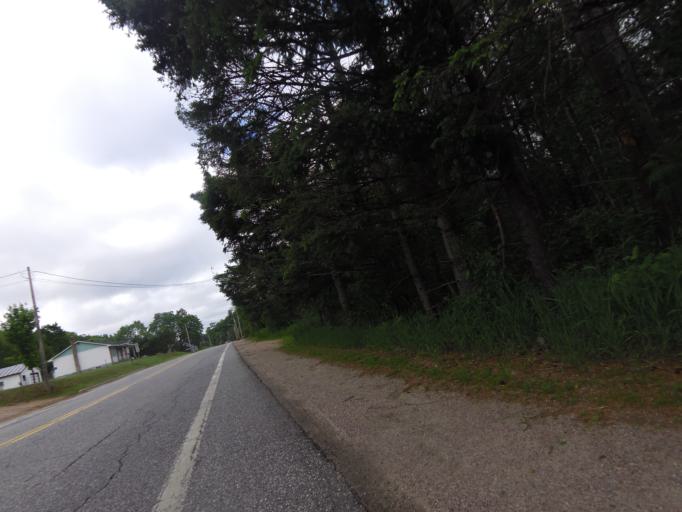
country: CA
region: Quebec
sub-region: Outaouais
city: Shawville
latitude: 45.8417
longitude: -76.4392
